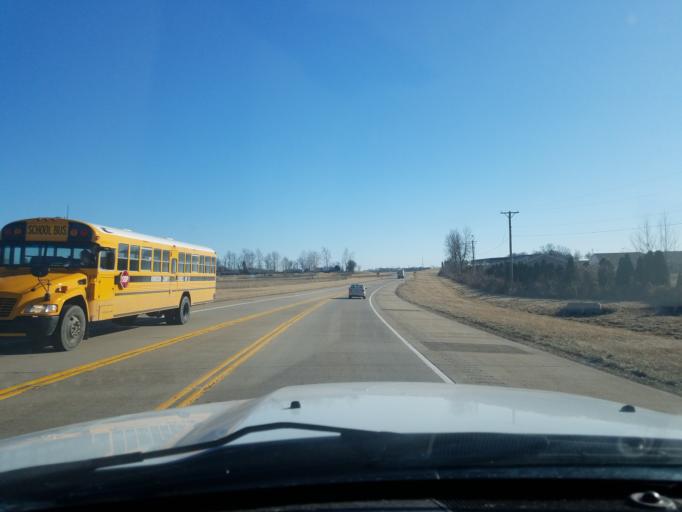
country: US
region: Kentucky
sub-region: Henderson County
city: Henderson
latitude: 37.7984
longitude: -87.6462
